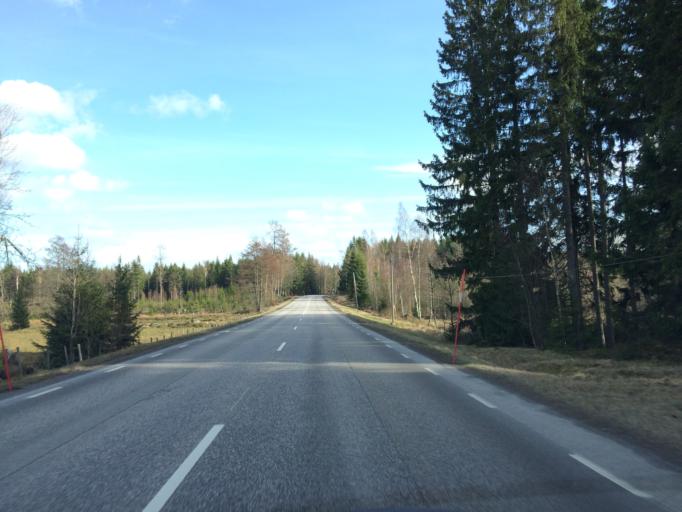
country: SE
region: Kronoberg
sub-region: Almhults Kommun
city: AElmhult
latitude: 56.6041
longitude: 14.0747
